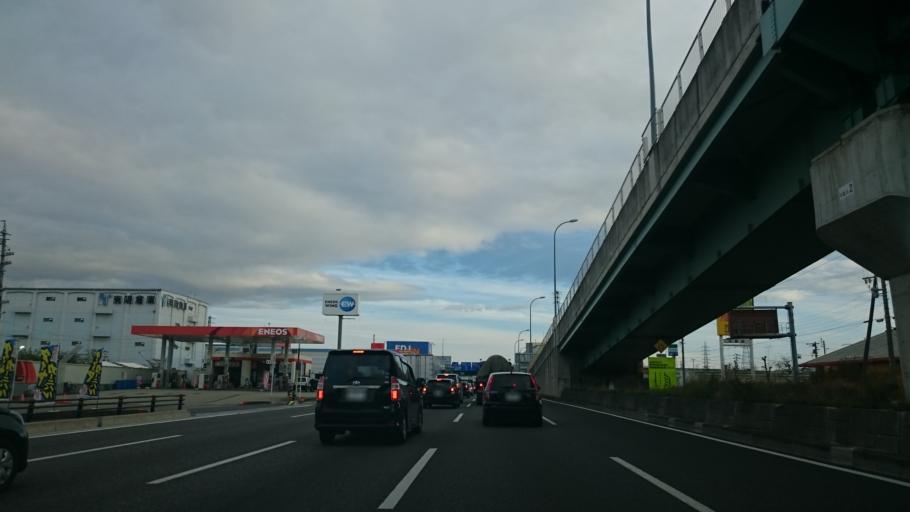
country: JP
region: Aichi
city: Komaki
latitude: 35.3039
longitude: 136.9109
